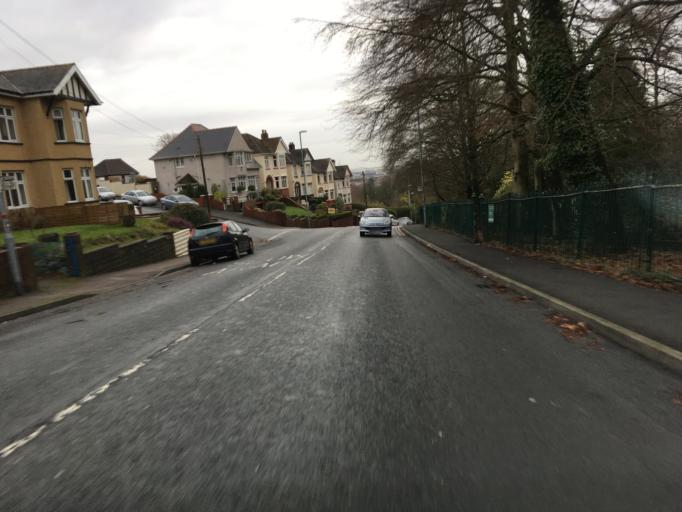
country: GB
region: Wales
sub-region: Newport
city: Caerleon
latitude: 51.5912
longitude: -2.9634
